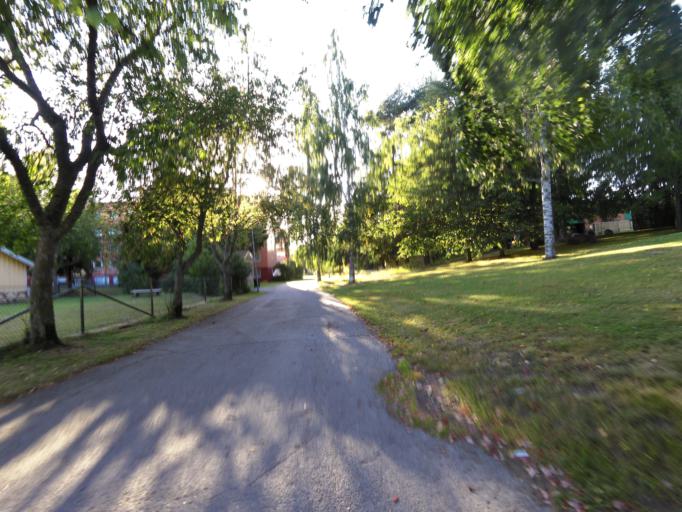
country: SE
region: Gaevleborg
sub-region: Gavle Kommun
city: Gavle
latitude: 60.6531
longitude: 17.1387
